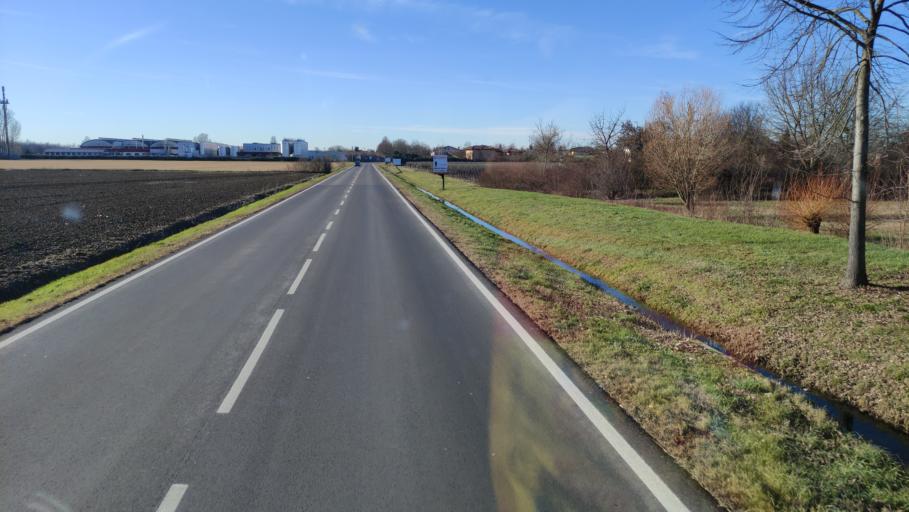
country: IT
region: Emilia-Romagna
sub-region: Provincia di Reggio Emilia
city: Campagnola Emilia
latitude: 44.8356
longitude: 10.7673
